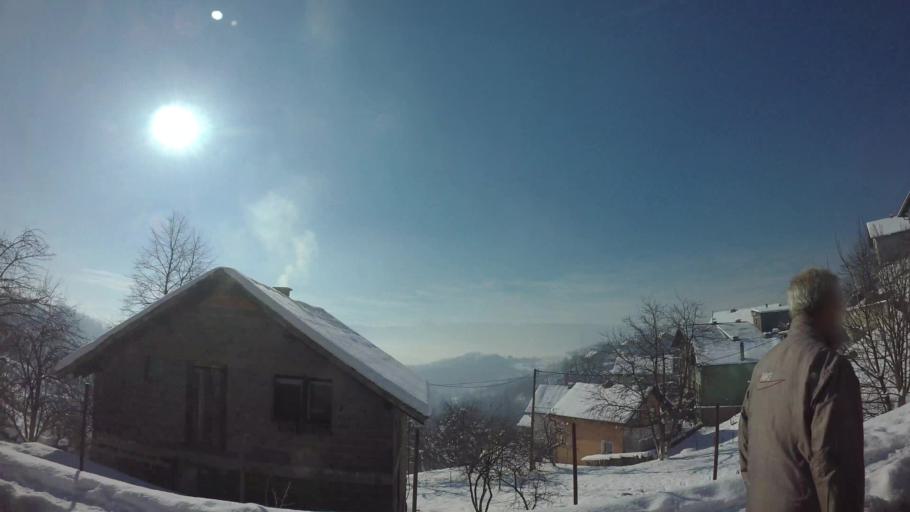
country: BA
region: Federation of Bosnia and Herzegovina
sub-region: Kanton Sarajevo
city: Sarajevo
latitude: 43.8398
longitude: 18.3774
